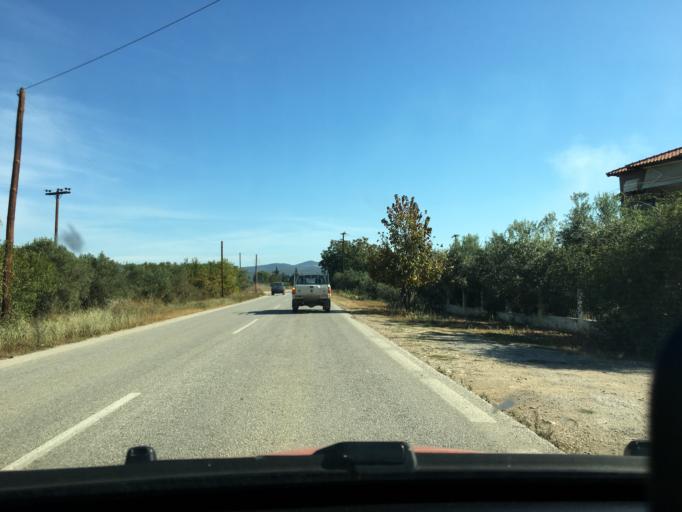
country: GR
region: Central Macedonia
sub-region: Nomos Chalkidikis
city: Ormylia
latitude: 40.2650
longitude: 23.5195
